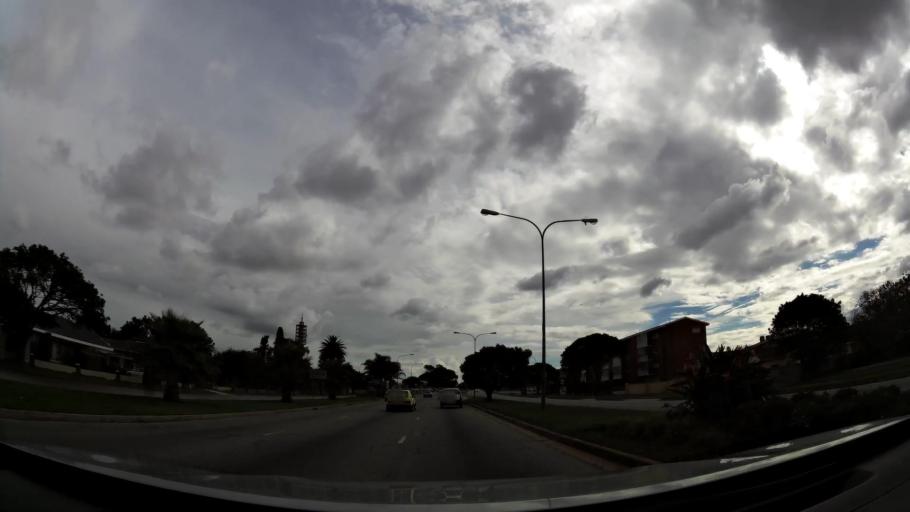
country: ZA
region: Eastern Cape
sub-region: Nelson Mandela Bay Metropolitan Municipality
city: Port Elizabeth
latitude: -33.9451
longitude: 25.5186
